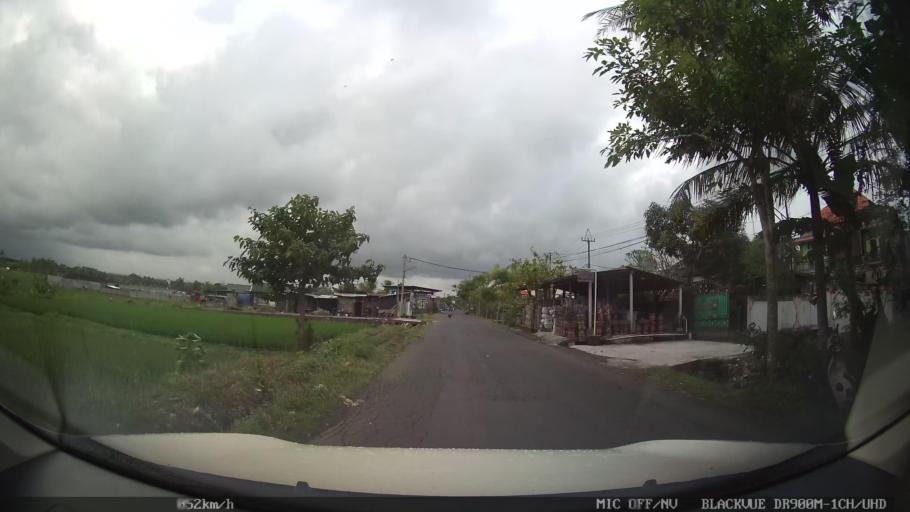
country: ID
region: Bali
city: Banjar Pekenjelodan
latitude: -8.5616
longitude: 115.1872
